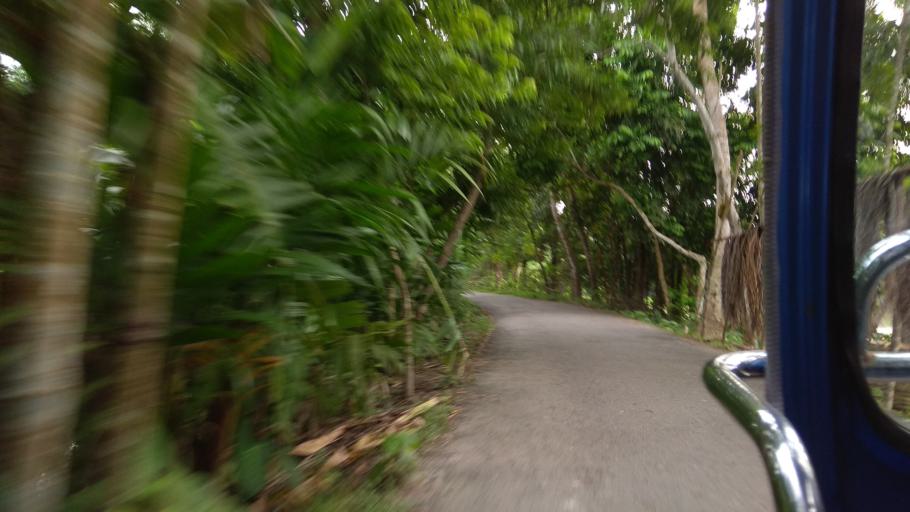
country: BD
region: Khulna
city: Kalia
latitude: 23.0367
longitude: 89.6578
